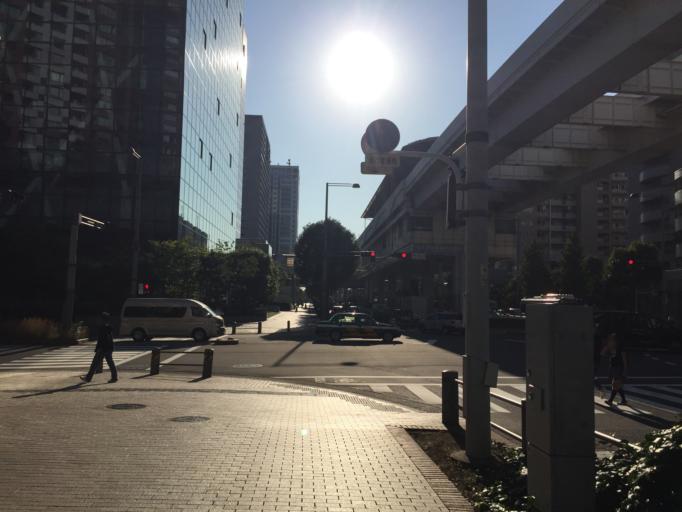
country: JP
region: Tokyo
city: Tokyo
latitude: 35.6303
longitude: 139.7798
